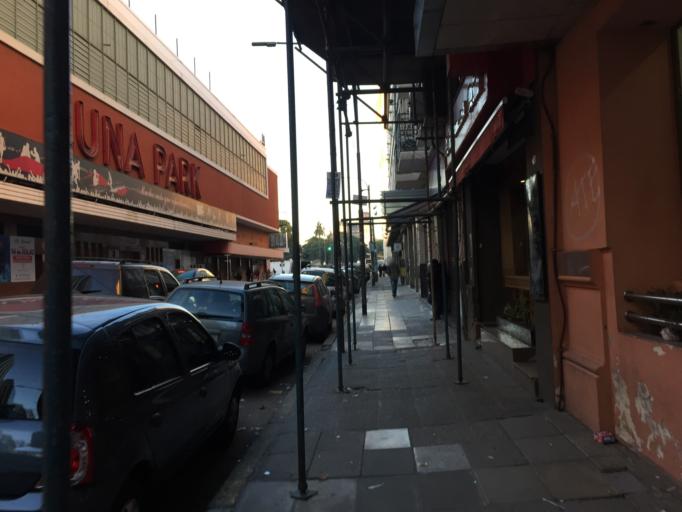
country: AR
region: Buenos Aires F.D.
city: Buenos Aires
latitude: -34.6019
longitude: -58.3691
